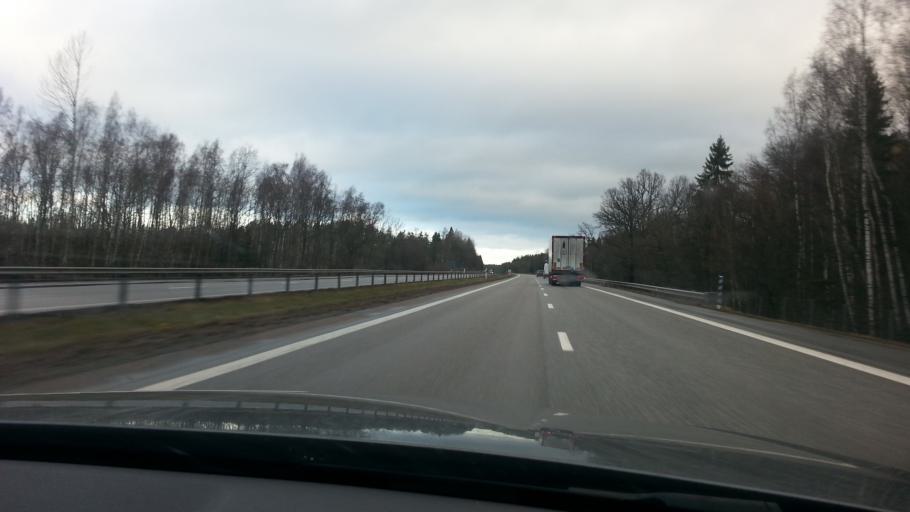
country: SE
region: Joenkoeping
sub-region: Jonkopings Kommun
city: Asa
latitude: 58.0932
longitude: 14.5504
